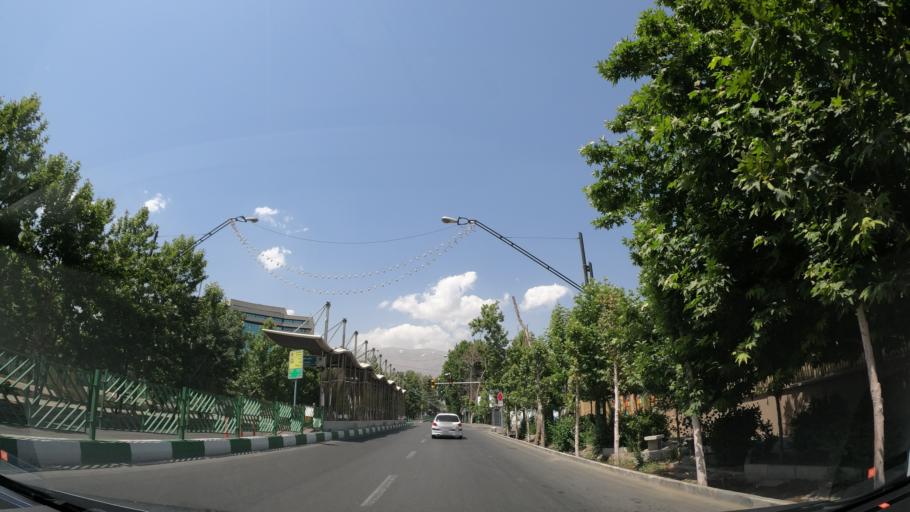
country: IR
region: Tehran
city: Tajrish
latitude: 35.7854
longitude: 51.4151
